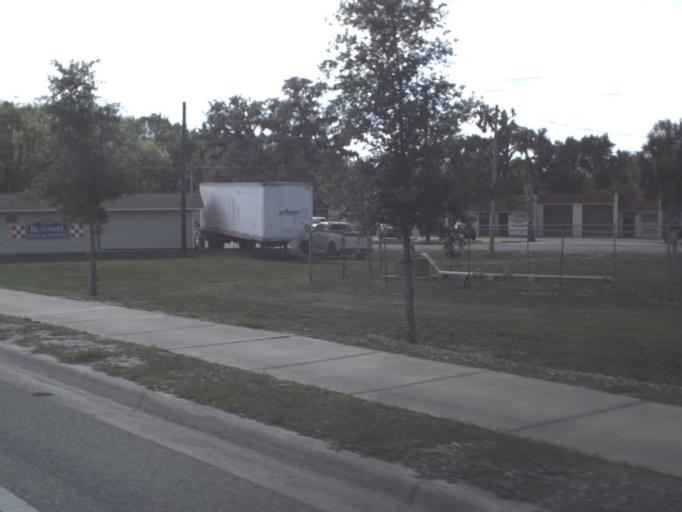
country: US
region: Florida
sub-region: Flagler County
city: Bunnell
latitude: 29.4744
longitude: -81.2486
